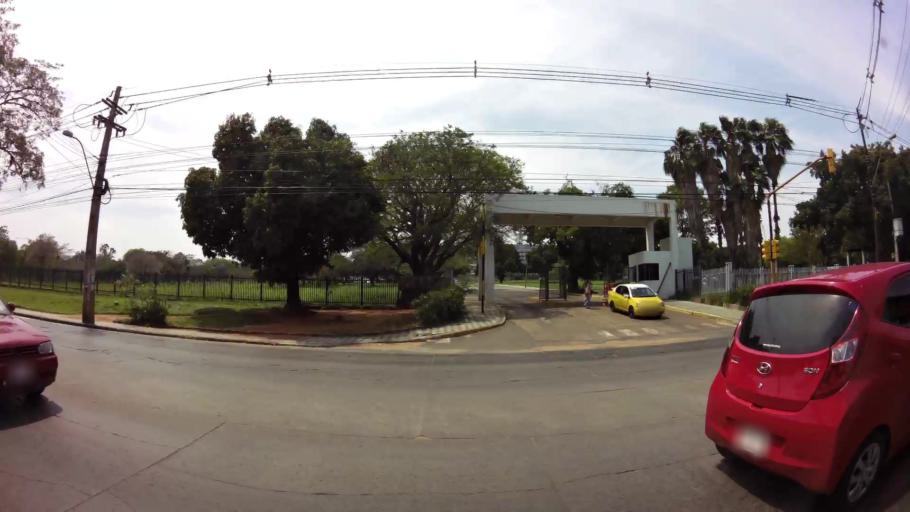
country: PY
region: Asuncion
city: Asuncion
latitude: -25.2708
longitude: -57.5841
